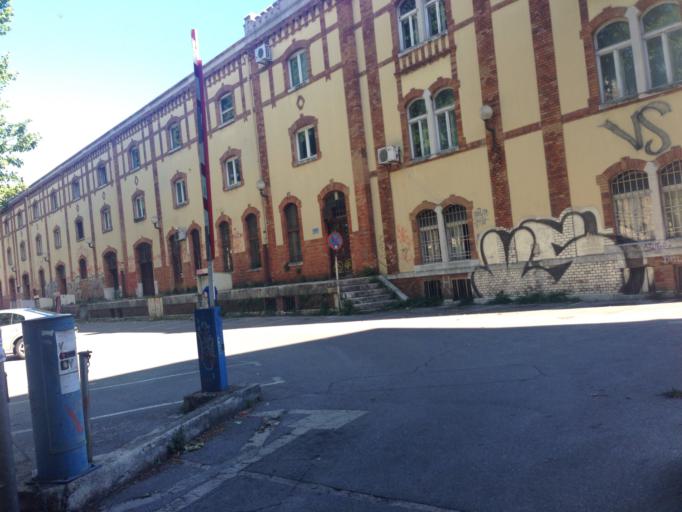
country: HR
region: Primorsko-Goranska
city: Drenova
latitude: 45.3302
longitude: 14.4324
